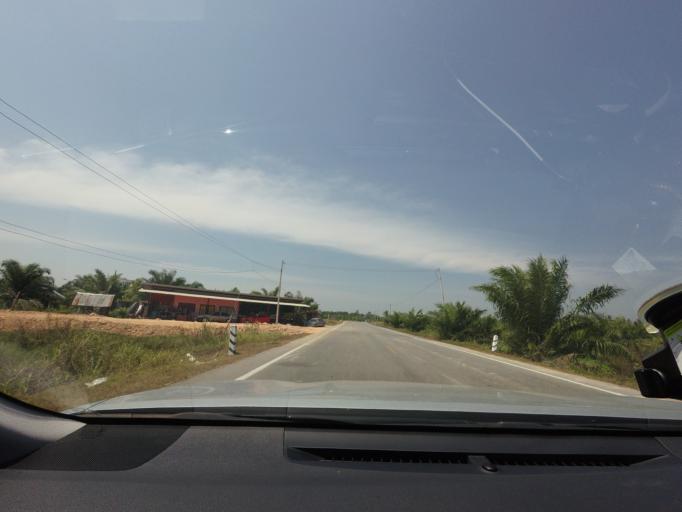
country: TH
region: Surat Thani
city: Tha Chang
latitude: 9.2139
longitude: 99.2019
